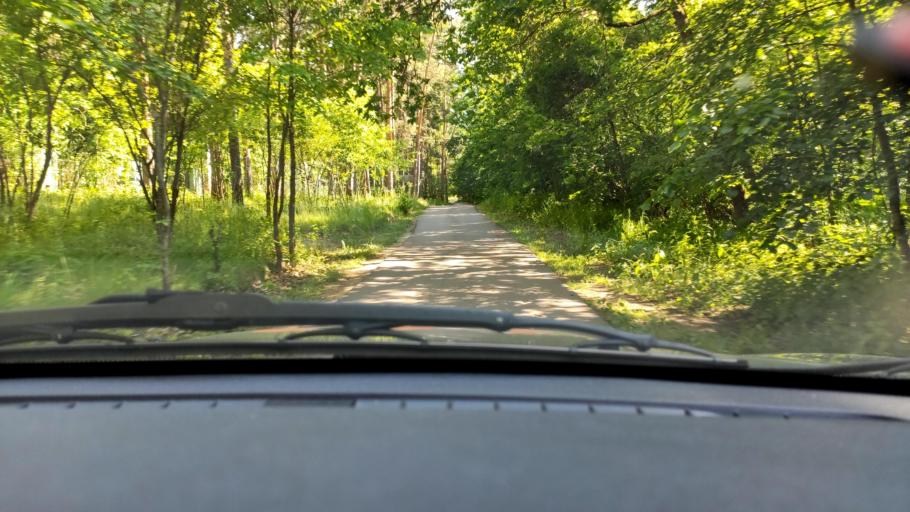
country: RU
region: Voronezj
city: Somovo
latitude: 51.8094
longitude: 39.3837
